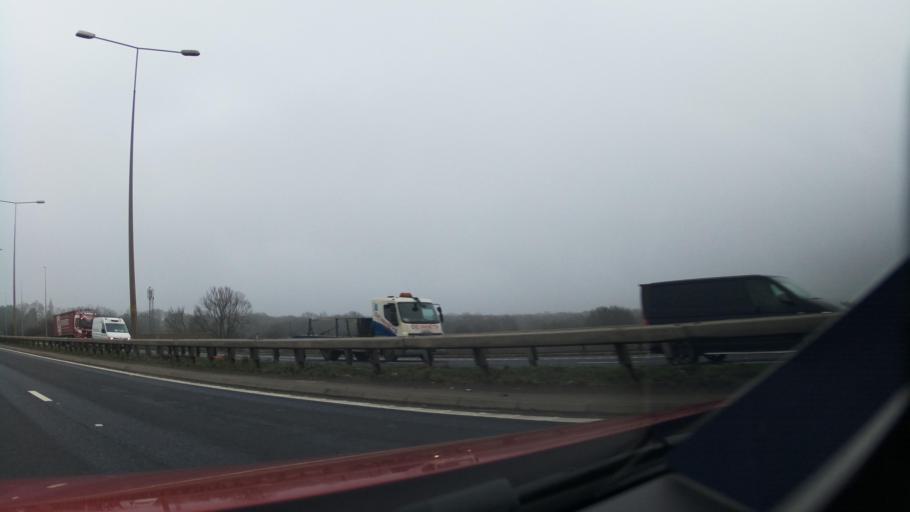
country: GB
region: England
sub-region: Borough of Wigan
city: Shevington
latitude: 53.5608
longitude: -2.7020
